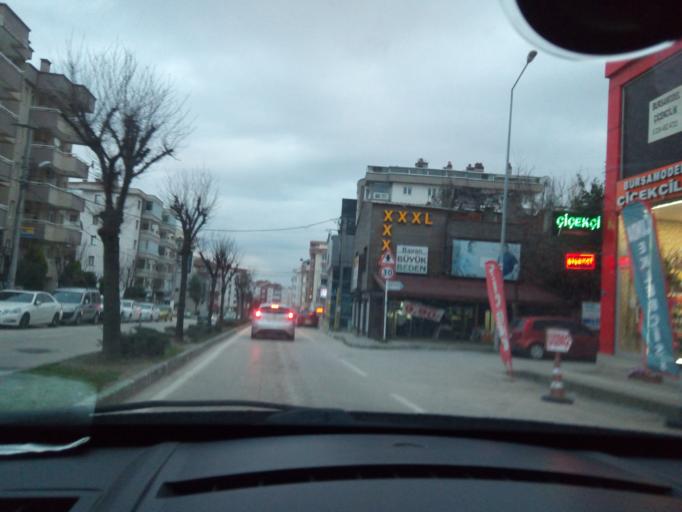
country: TR
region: Bursa
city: Yildirim
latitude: 40.2243
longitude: 28.9822
